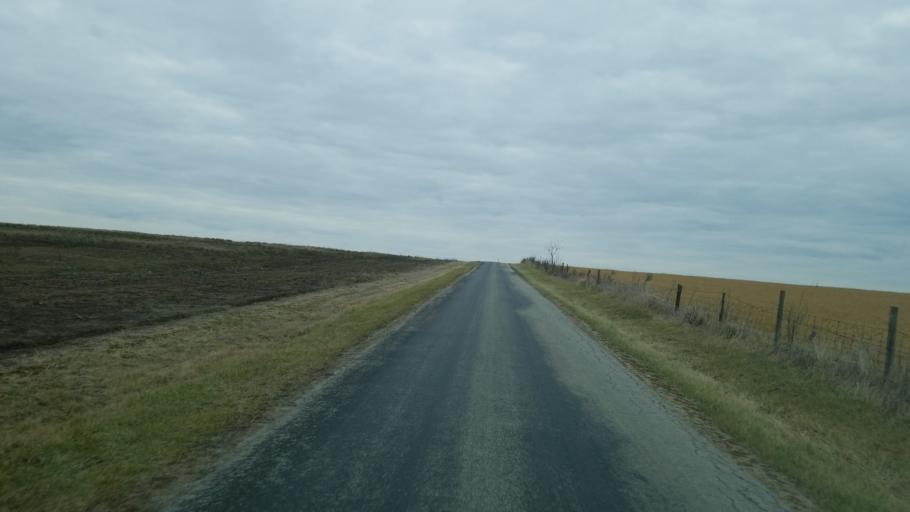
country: US
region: Ohio
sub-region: Highland County
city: Leesburg
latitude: 39.2592
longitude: -83.5281
